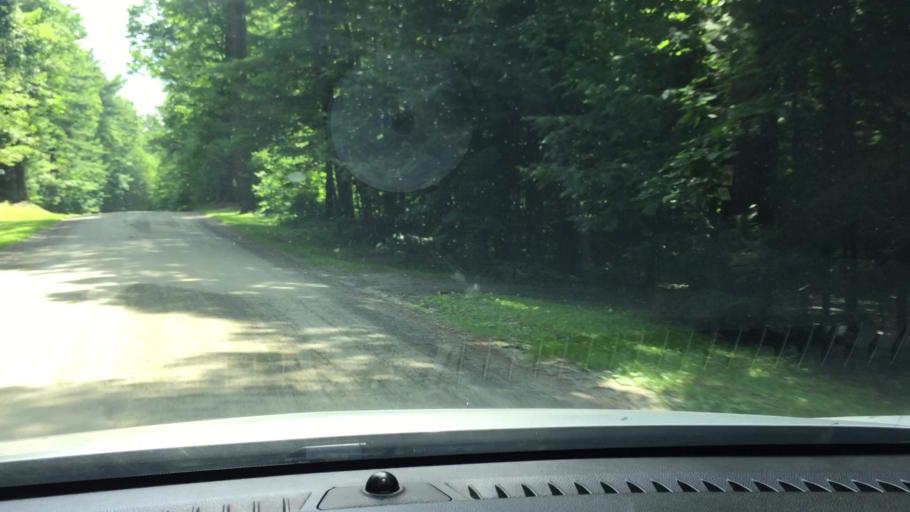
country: US
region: Massachusetts
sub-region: Berkshire County
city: Otis
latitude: 42.1861
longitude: -73.0943
